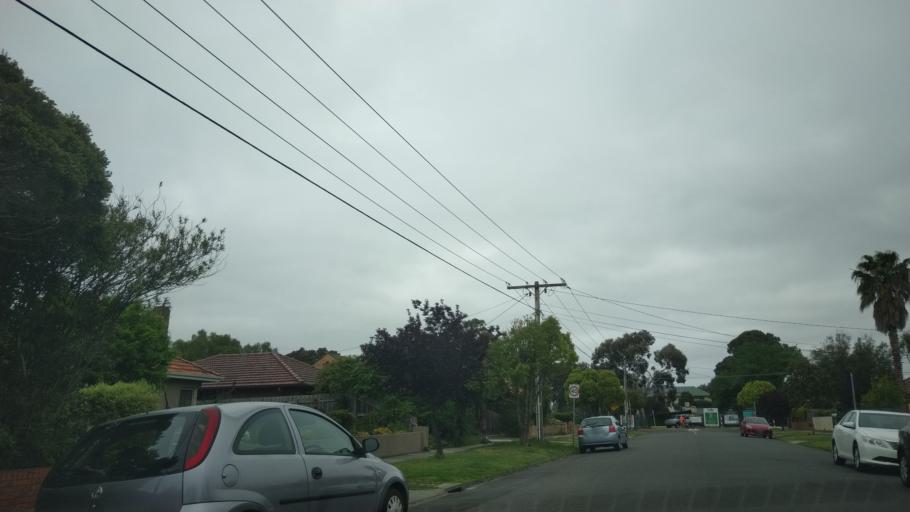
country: AU
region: Victoria
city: Hughesdale
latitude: -37.9037
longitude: 145.0781
